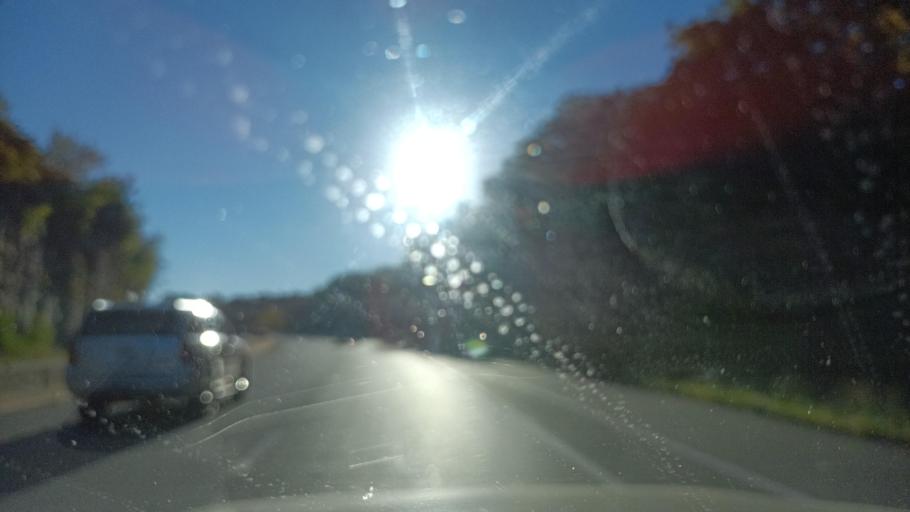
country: US
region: Missouri
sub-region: Boone County
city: Columbia
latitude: 38.9306
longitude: -92.3085
